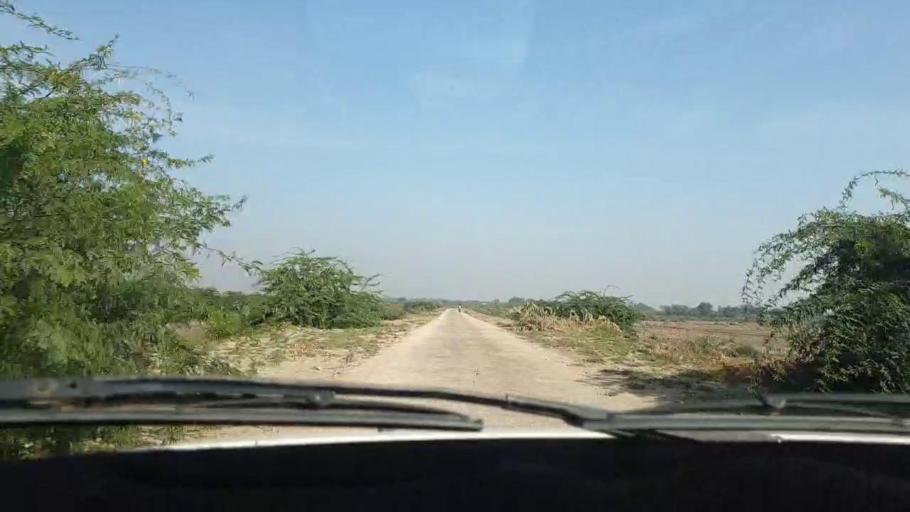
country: PK
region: Sindh
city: Tando Muhammad Khan
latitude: 24.9815
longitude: 68.4610
